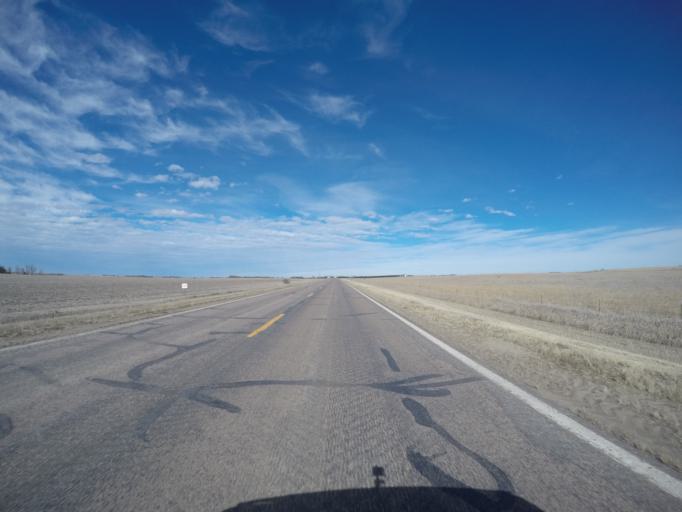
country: US
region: Nebraska
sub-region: Franklin County
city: Franklin
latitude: 40.1875
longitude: -98.9525
